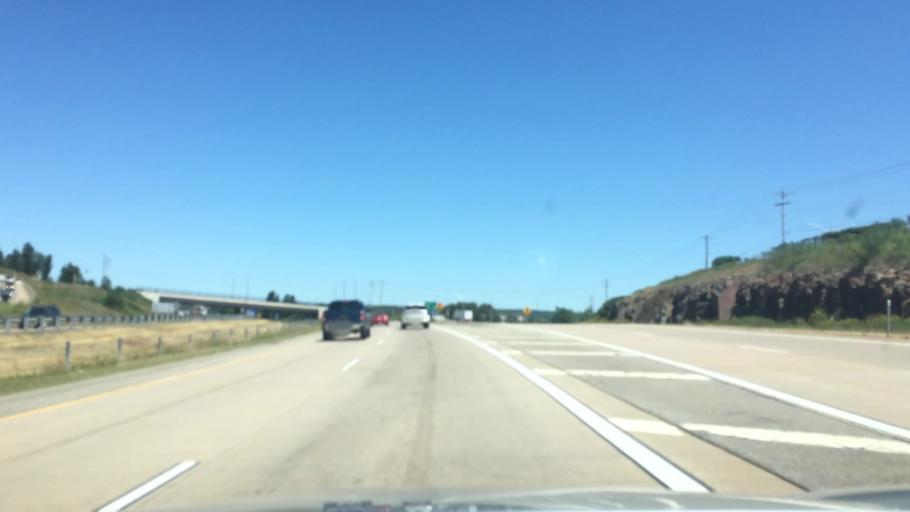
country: US
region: Wisconsin
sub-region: Marathon County
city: Wausau
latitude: 44.9667
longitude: -89.6562
